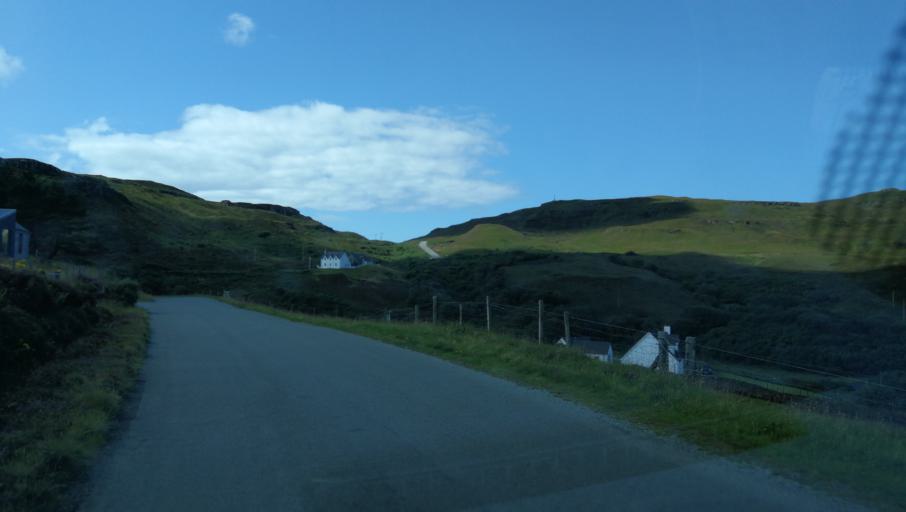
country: GB
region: Scotland
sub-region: Highland
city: Isle of Skye
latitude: 57.4526
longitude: -6.6616
